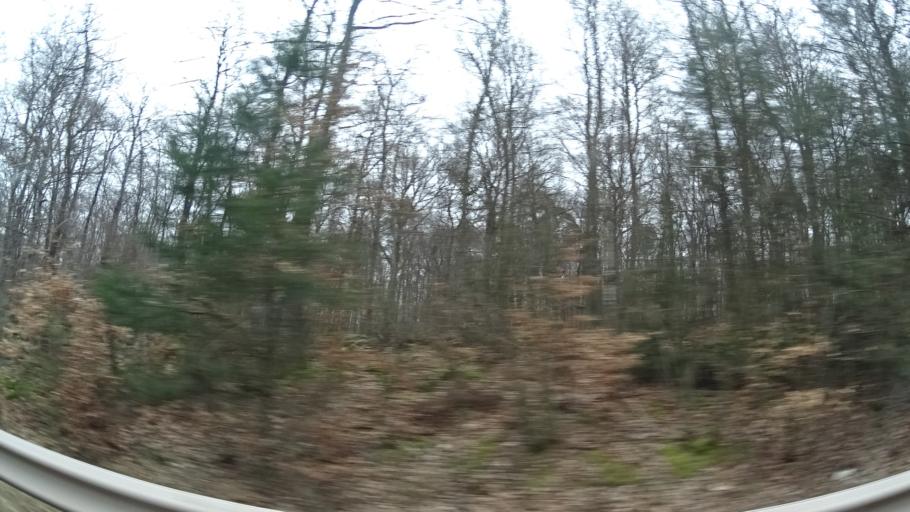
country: DE
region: Rheinland-Pfalz
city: Oberwiesen
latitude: 49.6634
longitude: 7.9738
